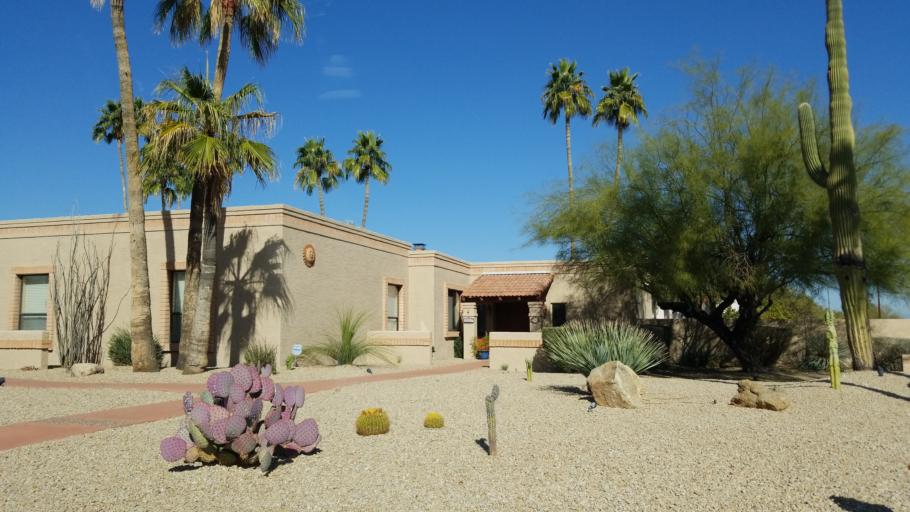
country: US
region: Arizona
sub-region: Maricopa County
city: Paradise Valley
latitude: 33.5863
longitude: -111.9822
